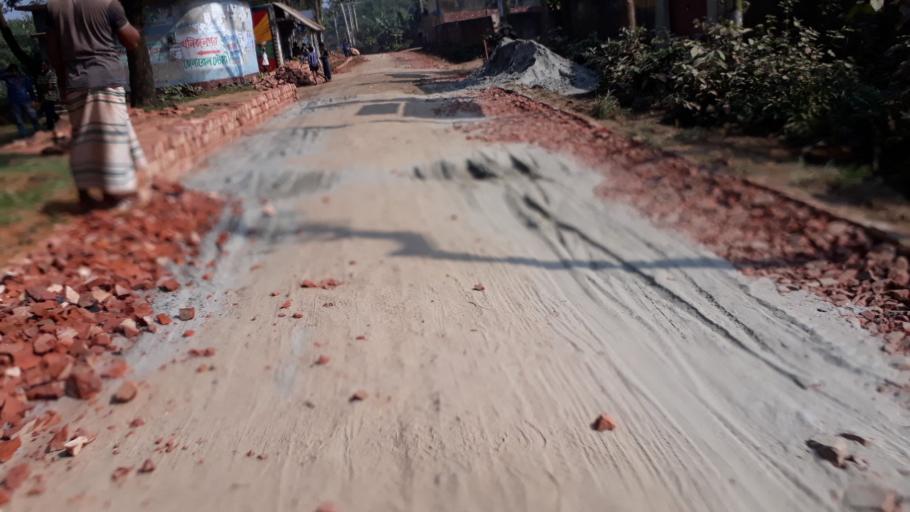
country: BD
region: Dhaka
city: Tungi
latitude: 23.8526
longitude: 90.2939
